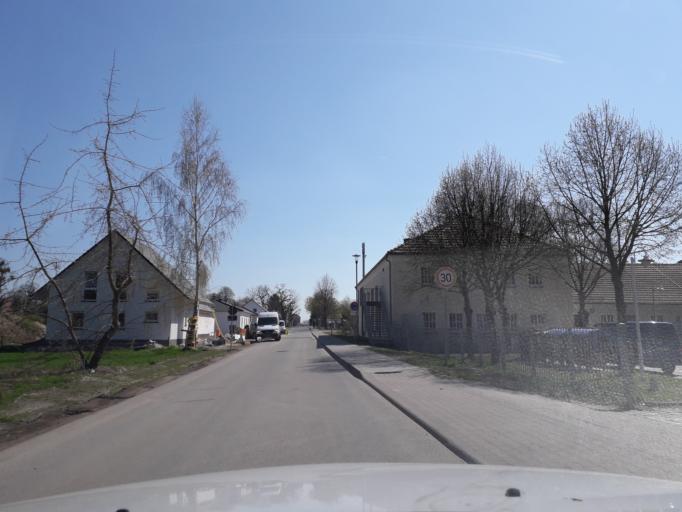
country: DE
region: Brandenburg
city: Wustermark
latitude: 52.5486
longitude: 12.9423
